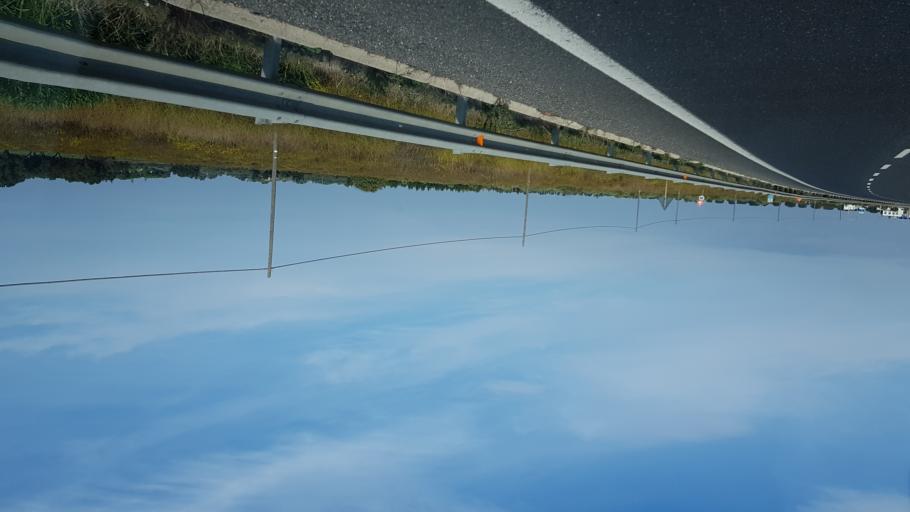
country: IT
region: Apulia
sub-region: Provincia di Brindisi
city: Brindisi
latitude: 40.6595
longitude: 17.8925
